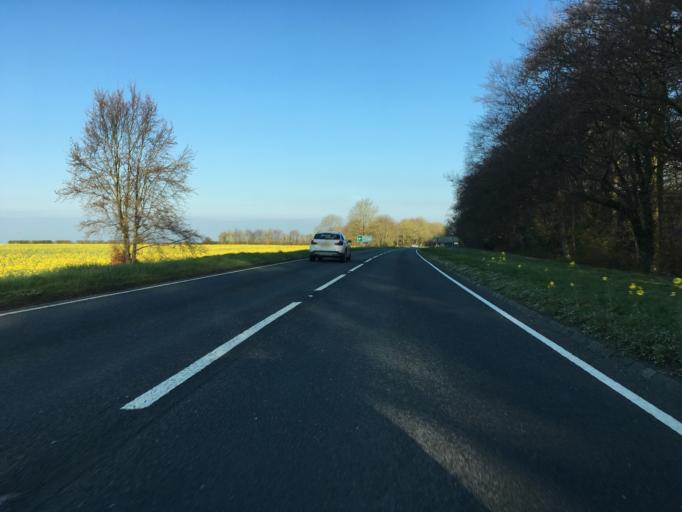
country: GB
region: England
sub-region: Gloucestershire
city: Bourton on the Water
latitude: 51.8159
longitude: -1.7504
